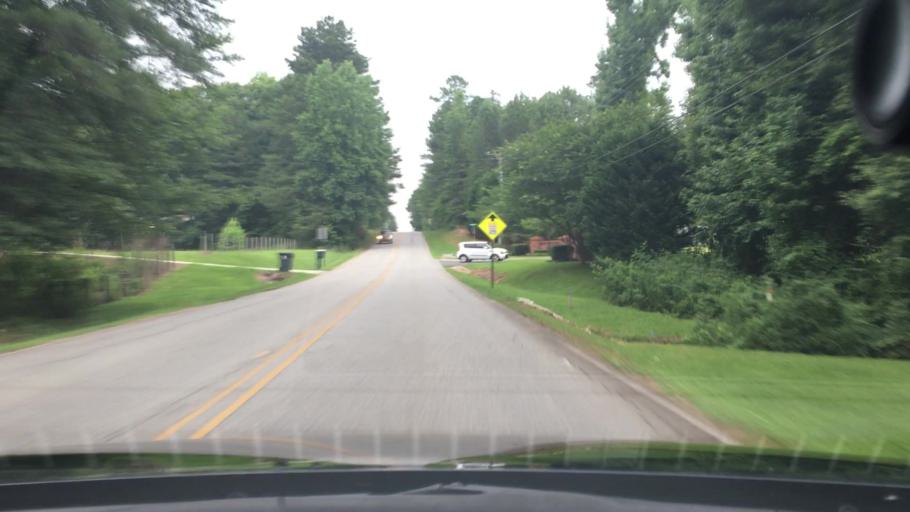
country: US
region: Georgia
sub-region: Coweta County
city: East Newnan
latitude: 33.3581
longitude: -84.7123
